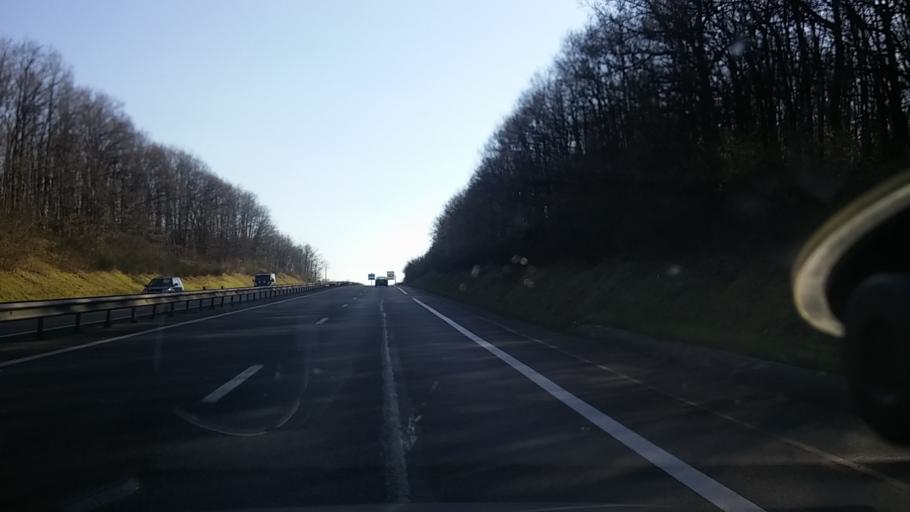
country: FR
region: Centre
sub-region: Departement de l'Indre
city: Saint-Marcel
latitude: 46.6230
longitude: 1.5457
